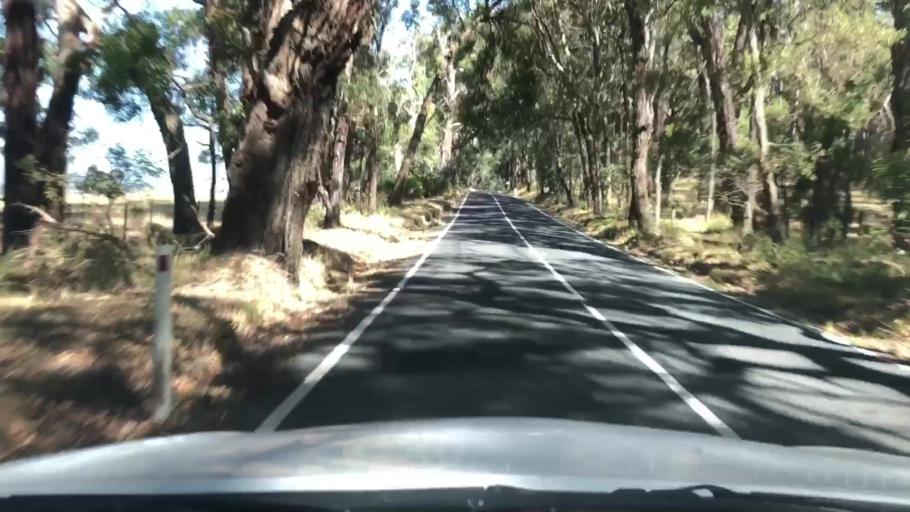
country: AU
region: Victoria
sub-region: Yarra Ranges
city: Macclesfield
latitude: -37.8470
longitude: 145.4855
